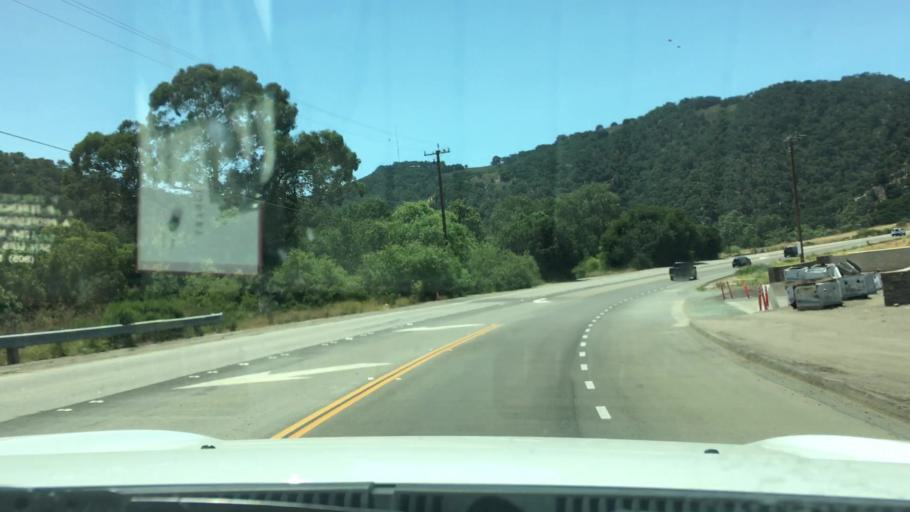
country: US
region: California
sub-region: San Luis Obispo County
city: Pismo Beach
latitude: 35.1656
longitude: -120.6300
